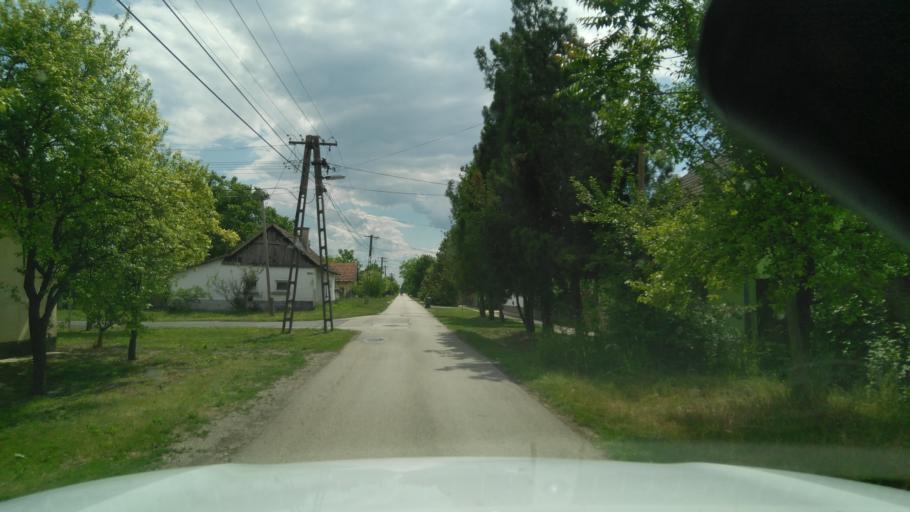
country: HU
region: Bekes
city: Magyarbanhegyes
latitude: 46.4591
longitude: 20.9562
